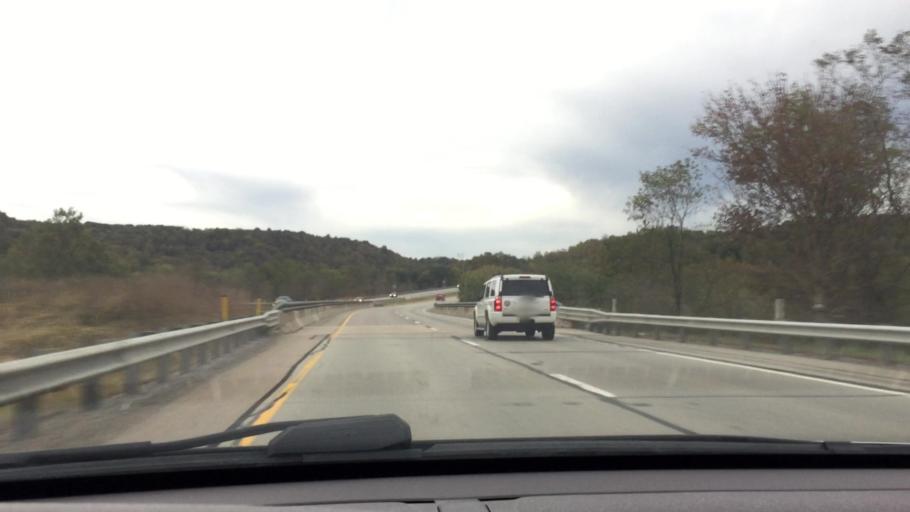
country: US
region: Pennsylvania
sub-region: Beaver County
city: Aliquippa
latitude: 40.6089
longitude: -80.3134
